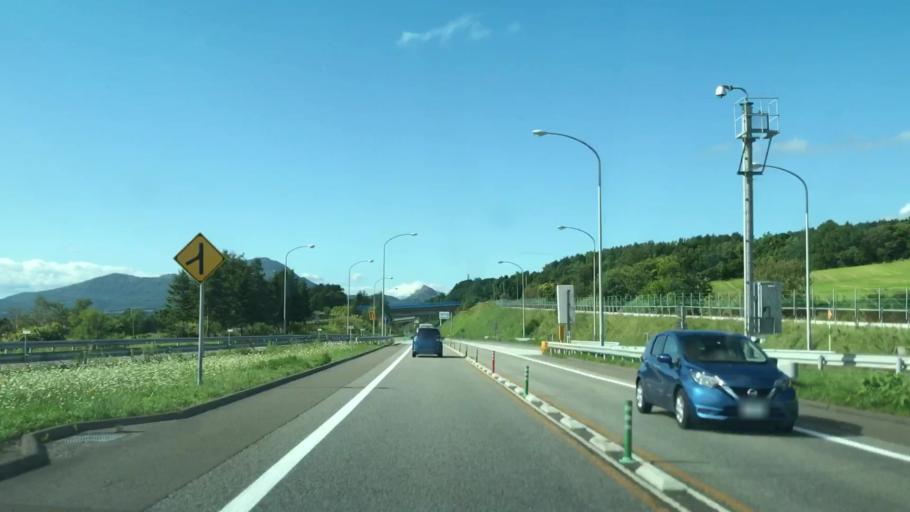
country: JP
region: Hokkaido
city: Date
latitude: 42.4674
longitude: 140.9080
